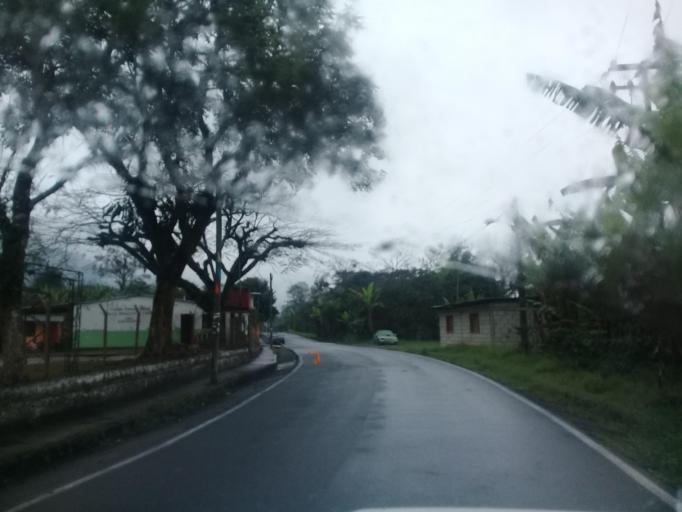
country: MX
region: Veracruz
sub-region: Amatlan de los Reyes
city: Centro de Readaptacion Social
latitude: 18.8031
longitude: -96.9515
